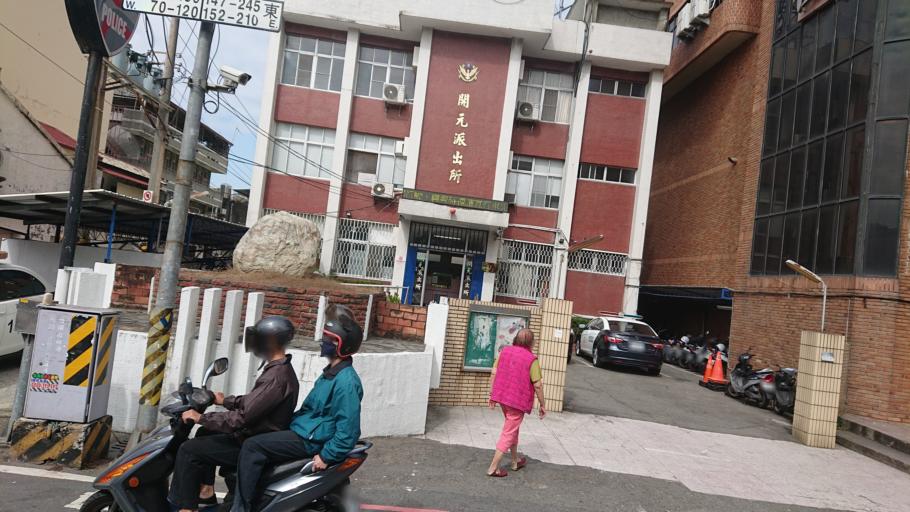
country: TW
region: Taiwan
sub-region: Tainan
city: Tainan
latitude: 23.0068
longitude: 120.2185
